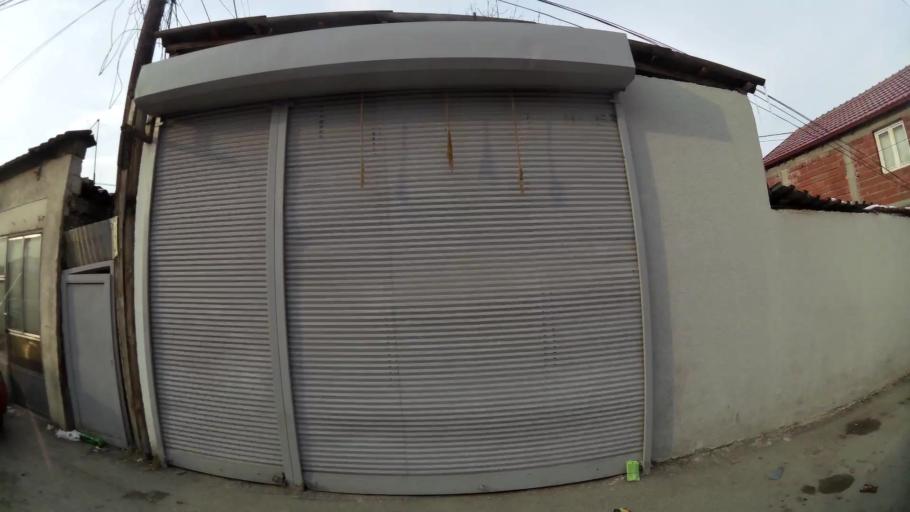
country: MK
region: Cair
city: Cair
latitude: 42.0165
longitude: 21.4389
